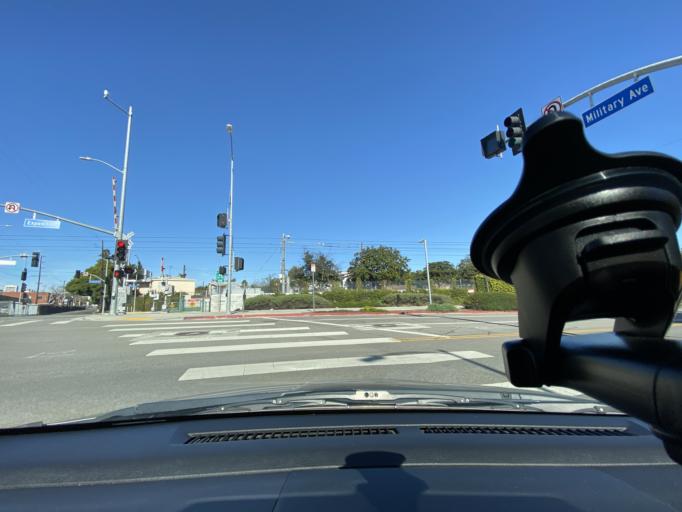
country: US
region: California
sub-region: Los Angeles County
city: Westwood, Los Angeles
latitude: 34.0356
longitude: -118.4309
